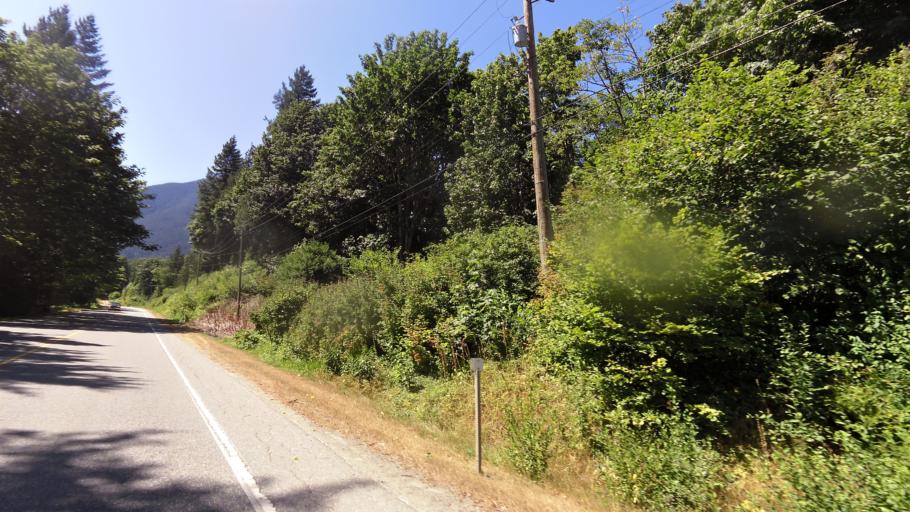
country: CA
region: British Columbia
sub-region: Fraser Valley Regional District
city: Chilliwack
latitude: 49.2438
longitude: -121.9915
